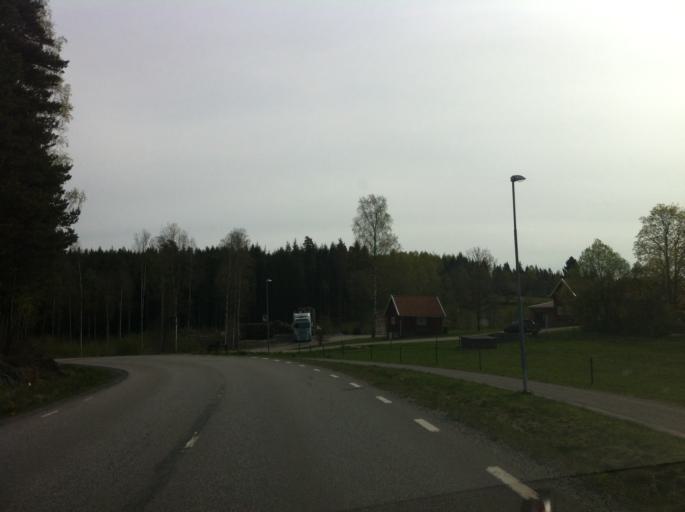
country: SE
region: Vaestra Goetaland
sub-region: Marks Kommun
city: Fritsla
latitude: 57.3971
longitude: 12.8138
